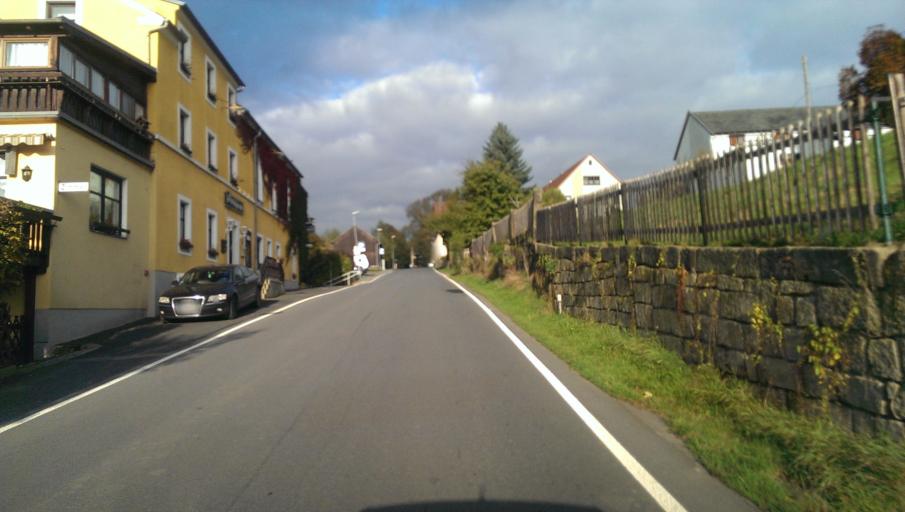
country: DE
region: Saxony
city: Porschdorf
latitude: 50.9421
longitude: 14.1260
